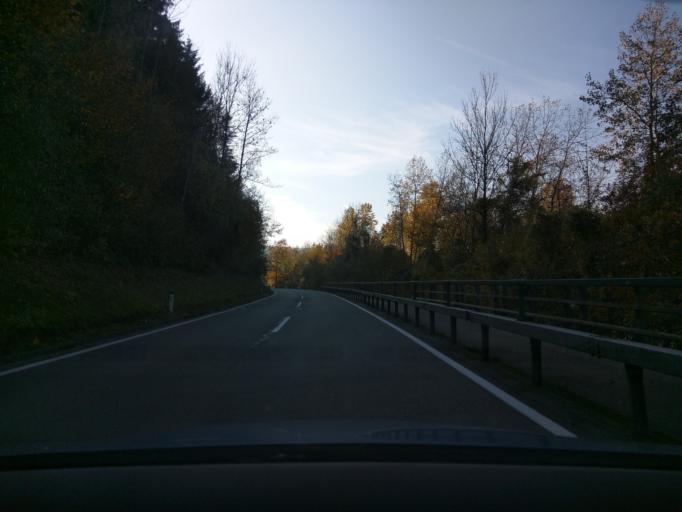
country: DE
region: Bavaria
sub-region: Lower Bavaria
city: Witzmannsberg
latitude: 48.5851
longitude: 13.5078
